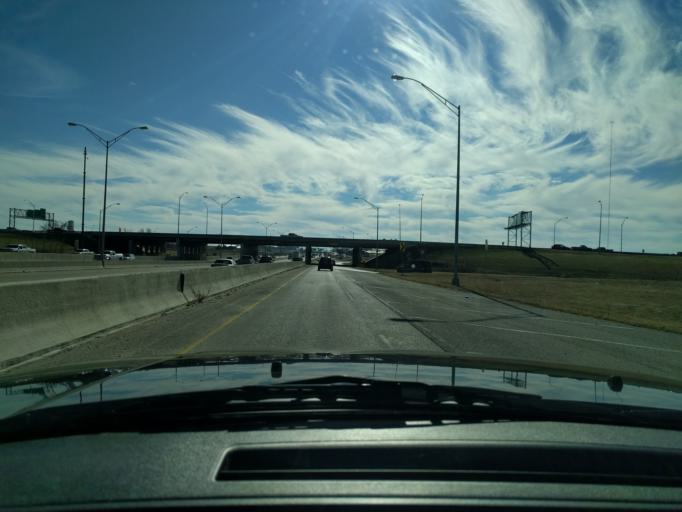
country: US
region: Oklahoma
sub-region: Cleveland County
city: Moore
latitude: 35.3930
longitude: -97.4954
